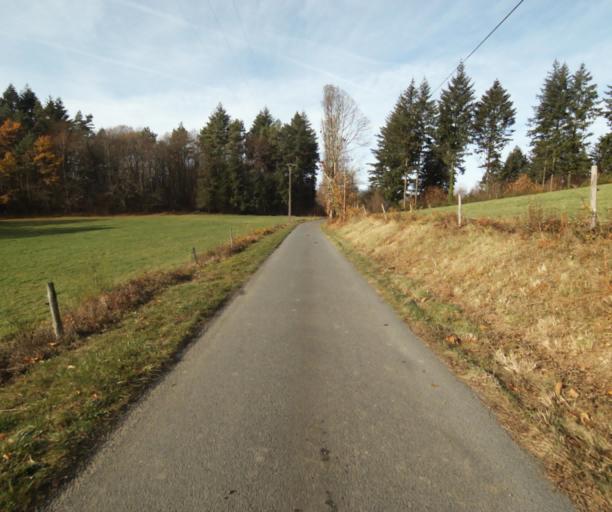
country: FR
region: Limousin
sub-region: Departement de la Correze
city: Sainte-Fortunade
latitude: 45.1987
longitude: 1.7518
